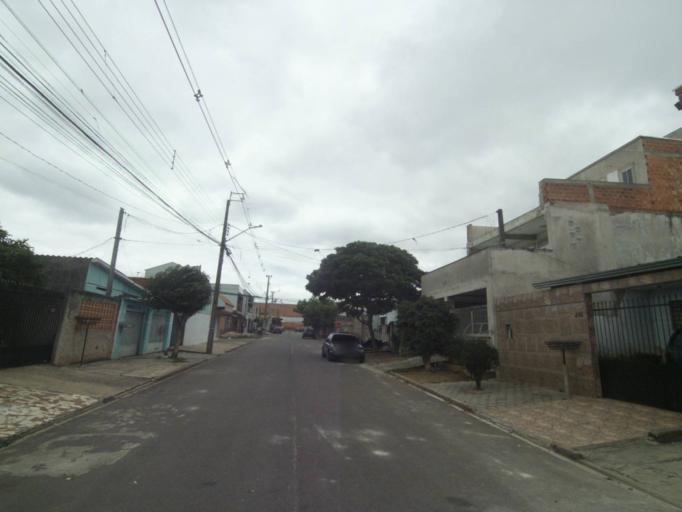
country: BR
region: Parana
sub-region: Sao Jose Dos Pinhais
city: Sao Jose dos Pinhais
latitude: -25.5561
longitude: -49.2656
